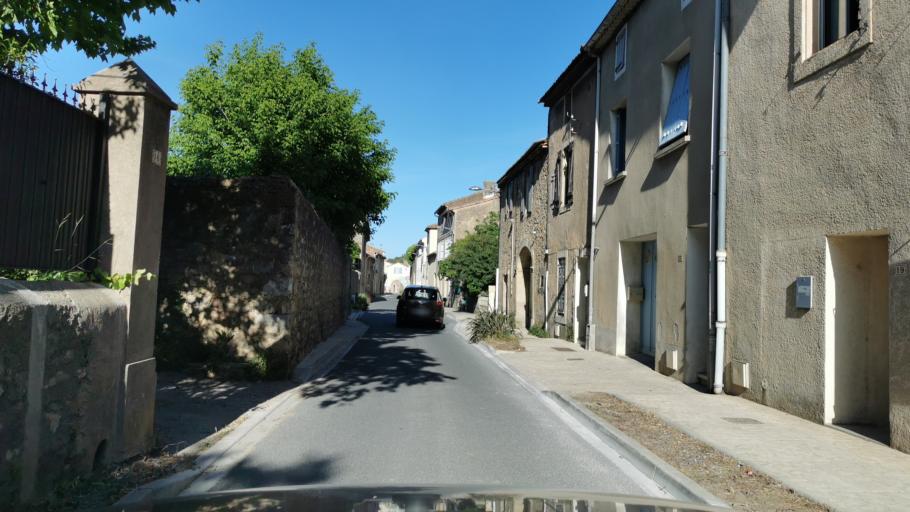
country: FR
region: Languedoc-Roussillon
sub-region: Departement de l'Aude
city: Nevian
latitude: 43.2121
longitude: 2.9020
